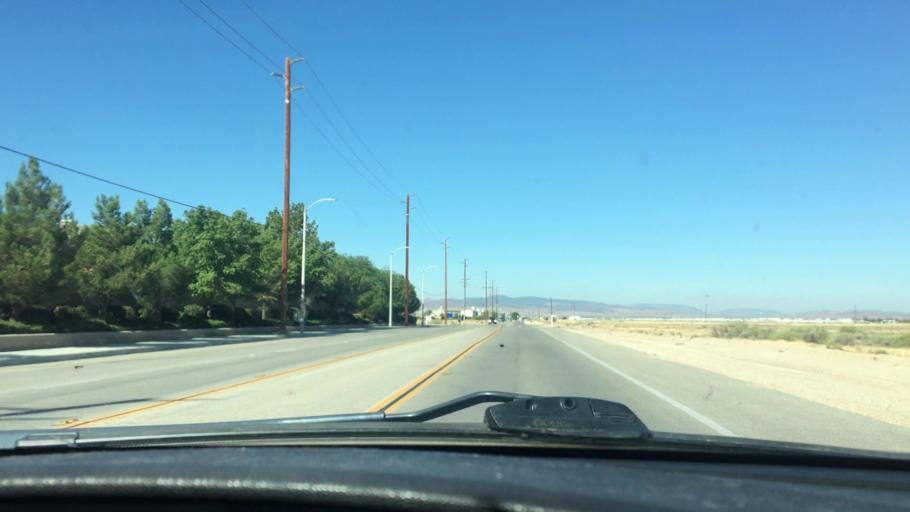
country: US
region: California
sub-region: Los Angeles County
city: Quartz Hill
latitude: 34.6894
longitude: -118.2043
